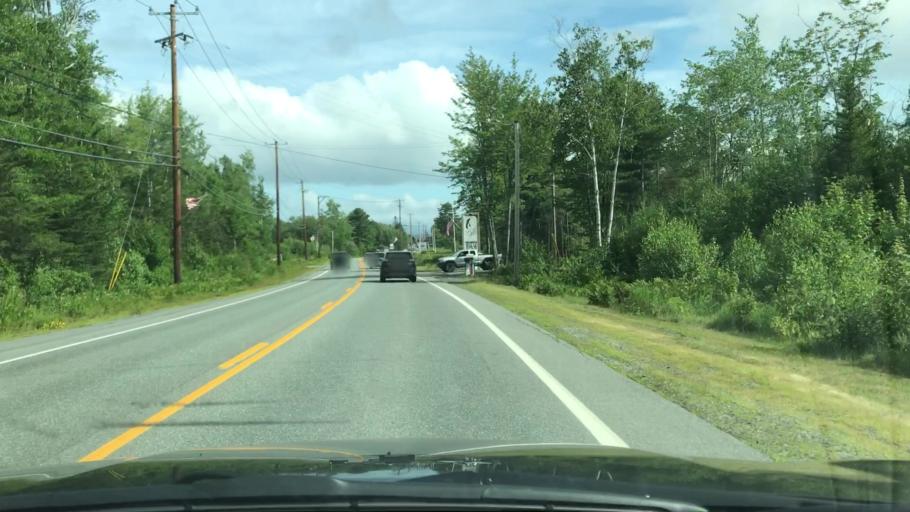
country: US
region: Maine
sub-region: Hancock County
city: Ellsworth
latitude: 44.5023
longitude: -68.3842
